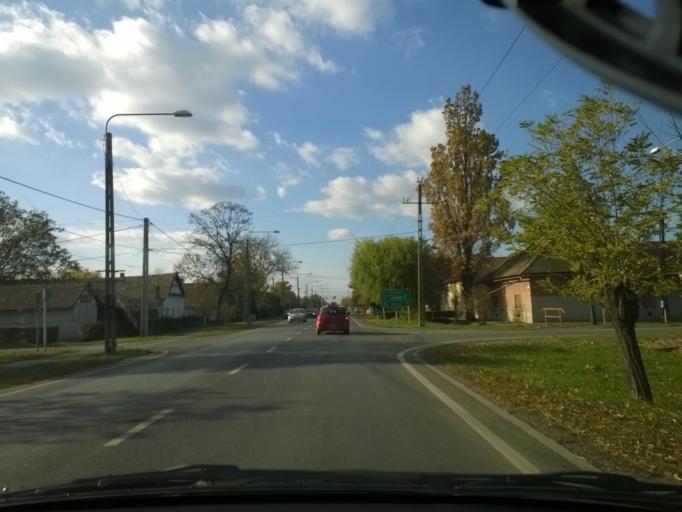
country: HU
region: Csongrad
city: Hodmezovasarhely
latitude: 46.4297
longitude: 20.3218
